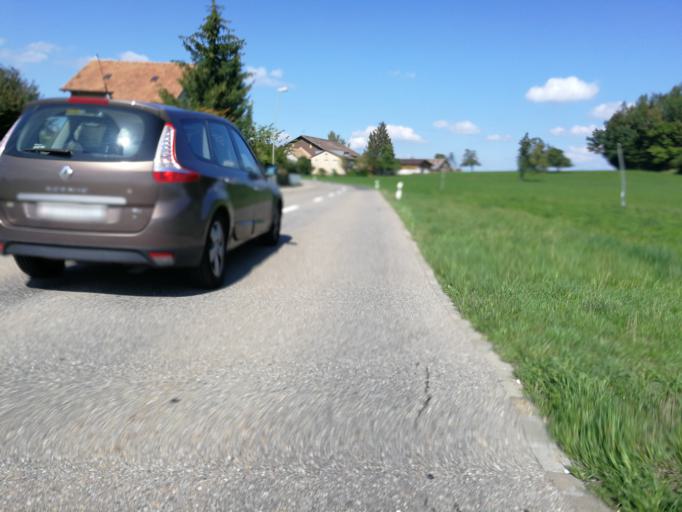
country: CH
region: Zurich
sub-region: Bezirk Horgen
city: Waedenswil / Eichweid
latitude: 47.2092
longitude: 8.6642
